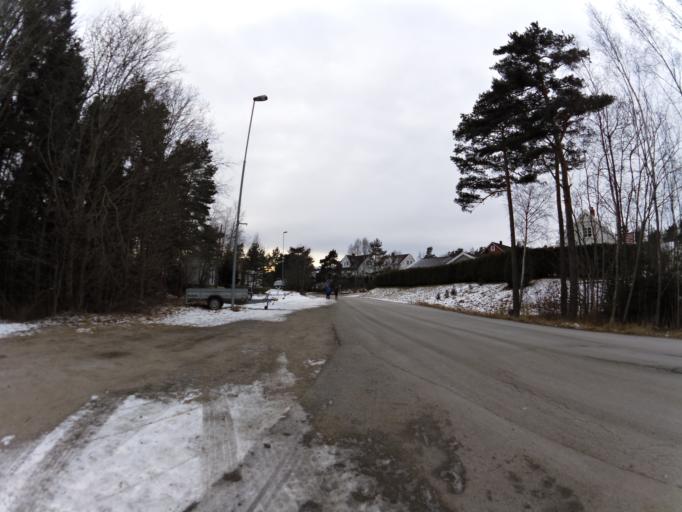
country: NO
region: Ostfold
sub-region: Fredrikstad
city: Fredrikstad
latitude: 59.1961
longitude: 10.8736
